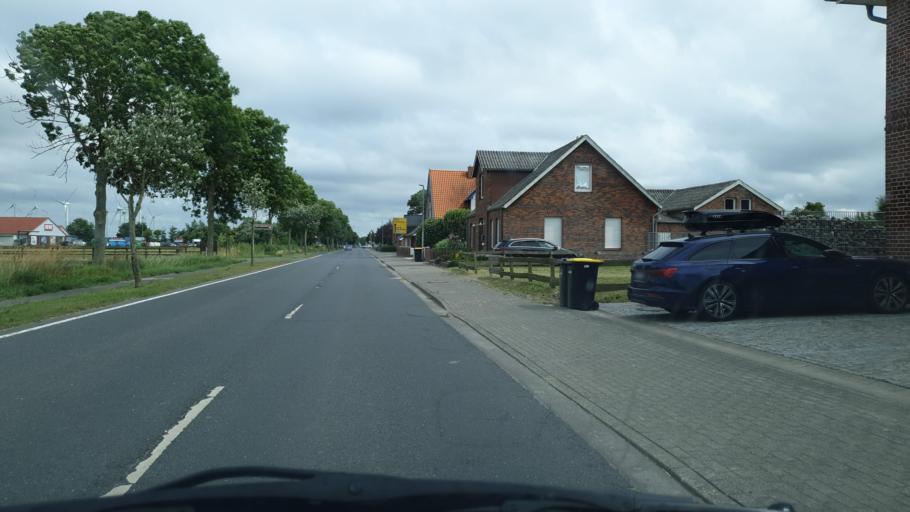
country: DE
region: Schleswig-Holstein
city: Friedrichskoog
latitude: 54.0153
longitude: 8.8939
